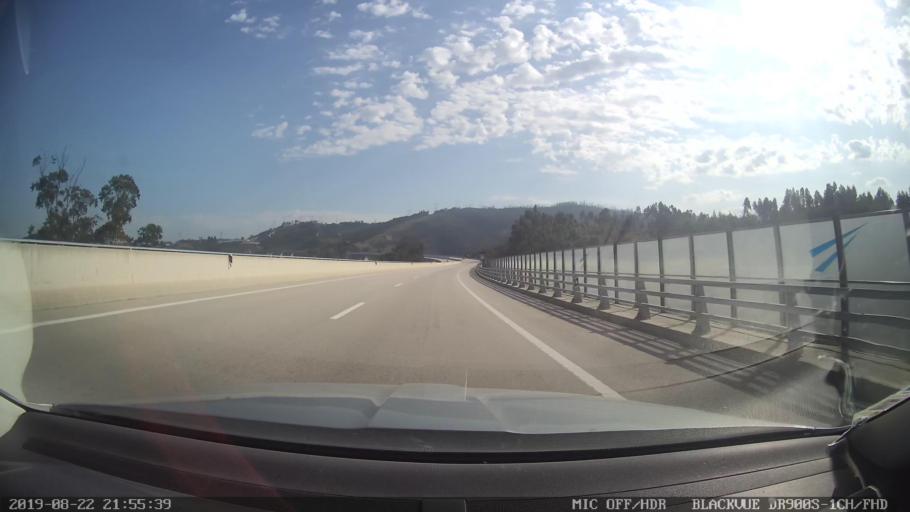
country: PT
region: Coimbra
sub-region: Coimbra
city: Coimbra
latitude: 40.1577
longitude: -8.3840
